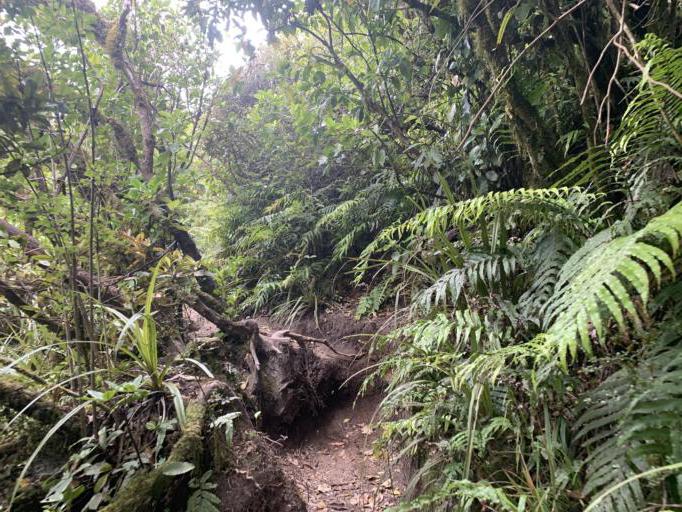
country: NZ
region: Waikato
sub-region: Taupo District
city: Taupo
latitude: -38.6948
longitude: 176.1621
